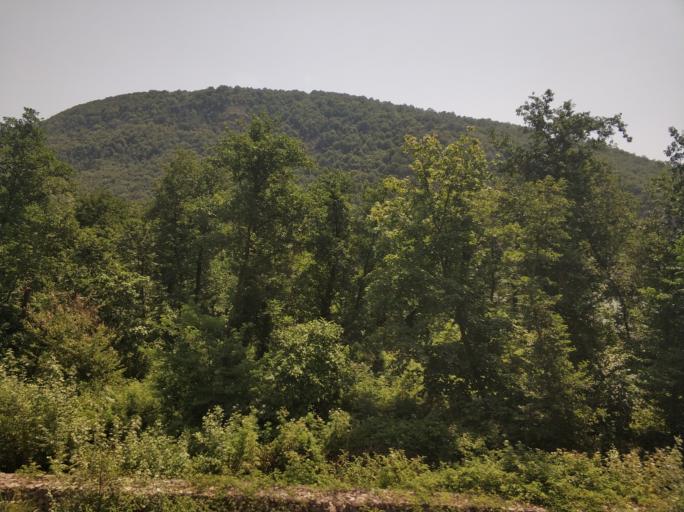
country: IR
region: Gilan
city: Pa'in-e Bazar-e Rudbar
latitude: 36.9780
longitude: 49.5548
